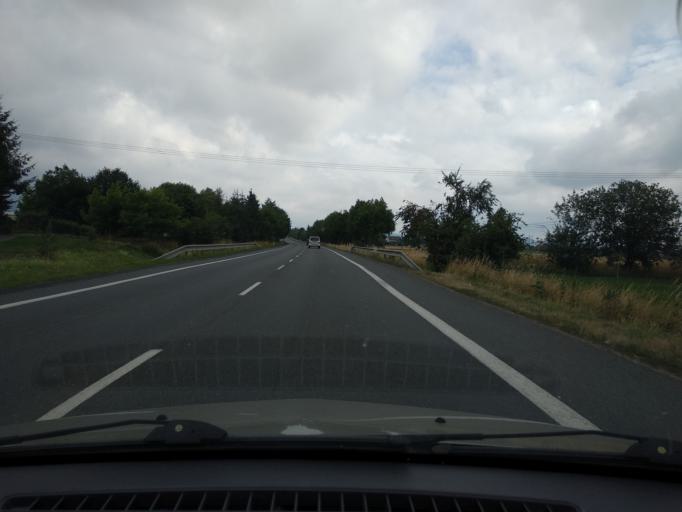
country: CZ
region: Olomoucky
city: Zabreh
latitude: 49.8811
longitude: 16.8933
